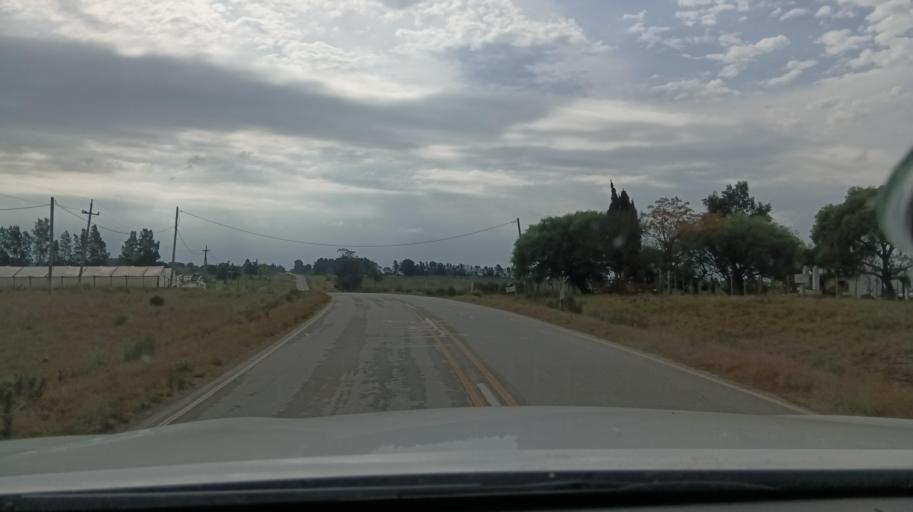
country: UY
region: Canelones
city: Sauce
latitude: -34.6442
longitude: -56.1062
